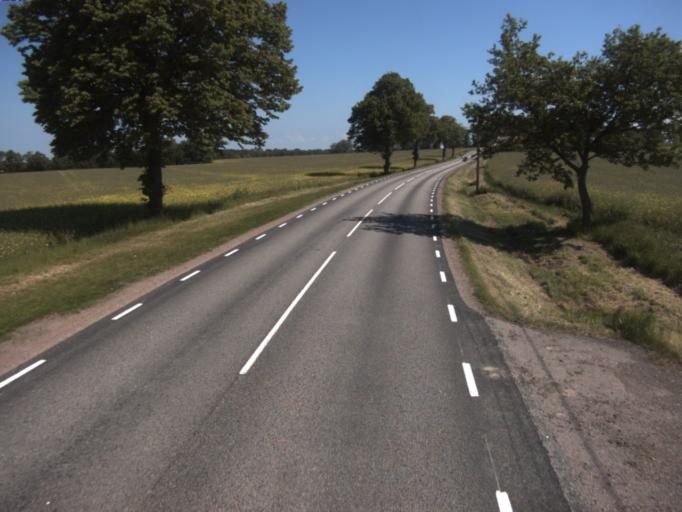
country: SE
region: Skane
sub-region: Helsingborg
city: Barslov
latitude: 56.0384
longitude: 12.7929
